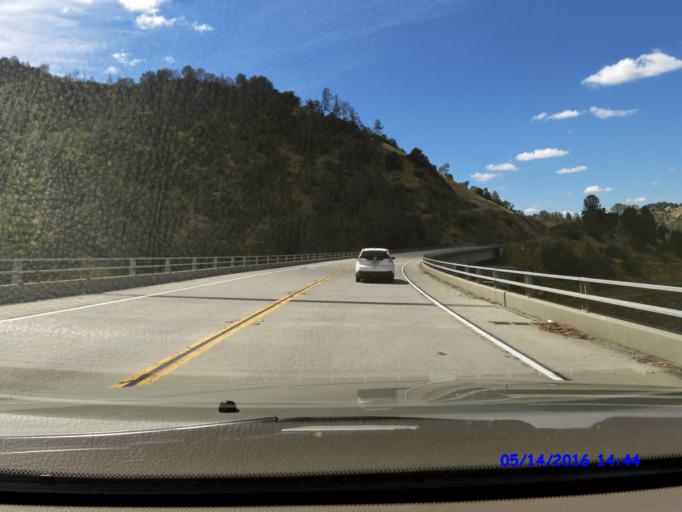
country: US
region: California
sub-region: Tuolumne County
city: Jamestown
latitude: 37.8395
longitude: -120.3786
